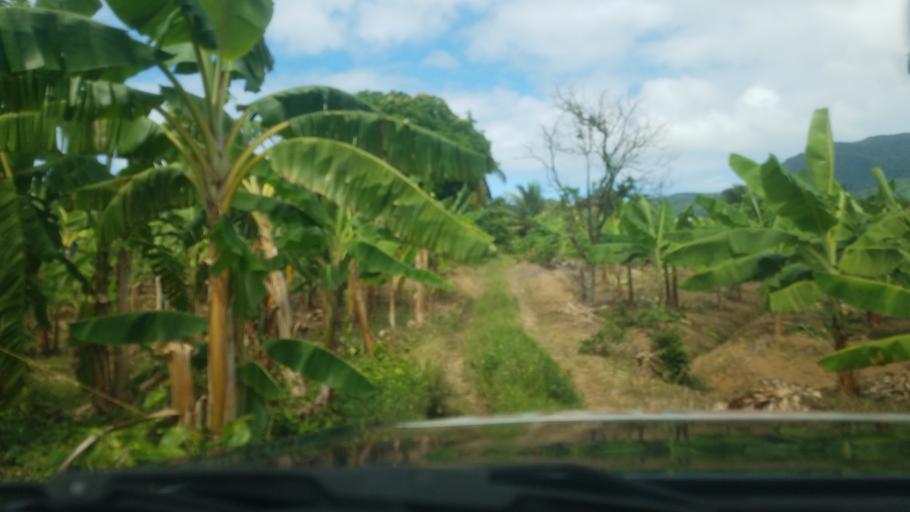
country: LC
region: Dennery Quarter
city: Dennery
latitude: 13.9332
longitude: -60.9202
